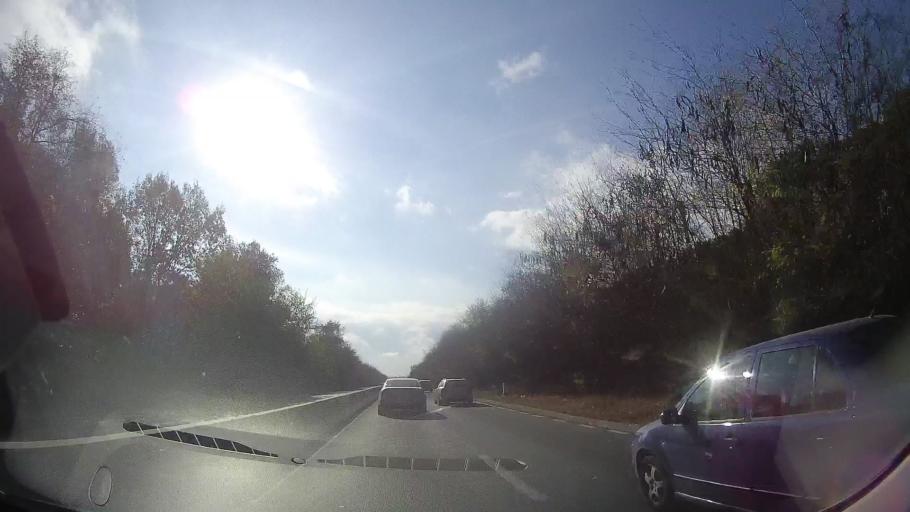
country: RO
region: Constanta
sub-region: Comuna Agigea
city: Agigea
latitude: 44.1269
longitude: 28.6152
